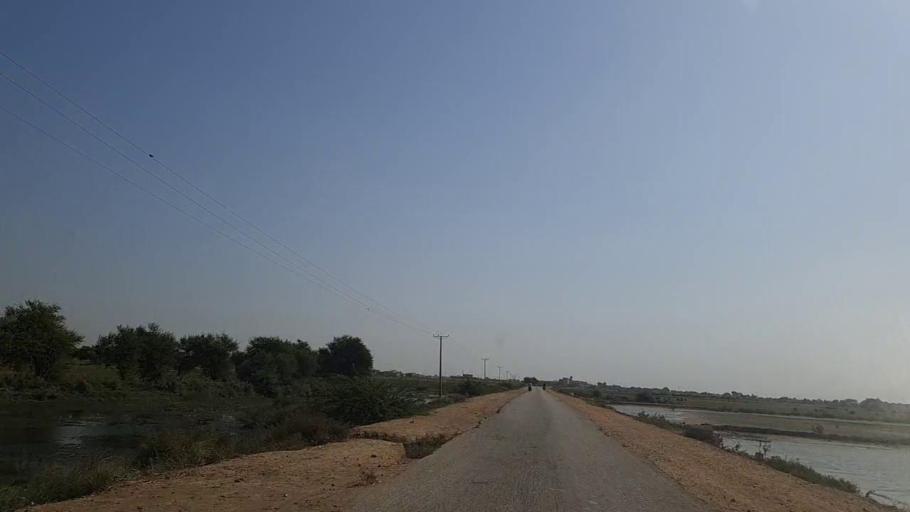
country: PK
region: Sindh
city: Mirpur Batoro
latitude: 24.6267
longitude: 68.2941
